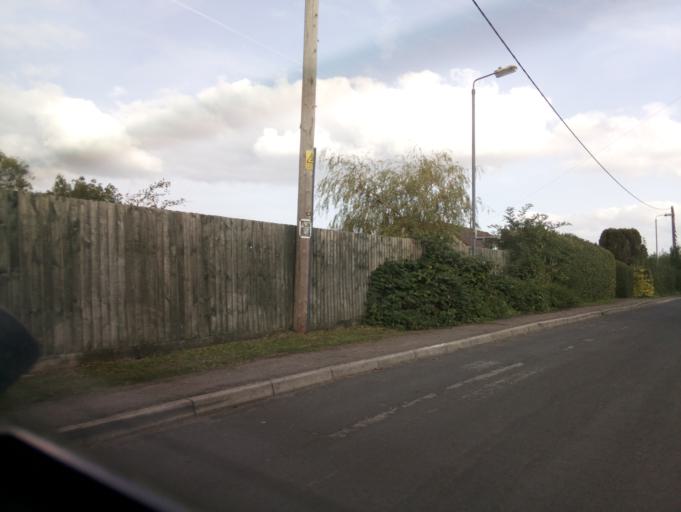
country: GB
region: England
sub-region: South Gloucestershire
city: Almondsbury
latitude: 51.5642
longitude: -2.5528
